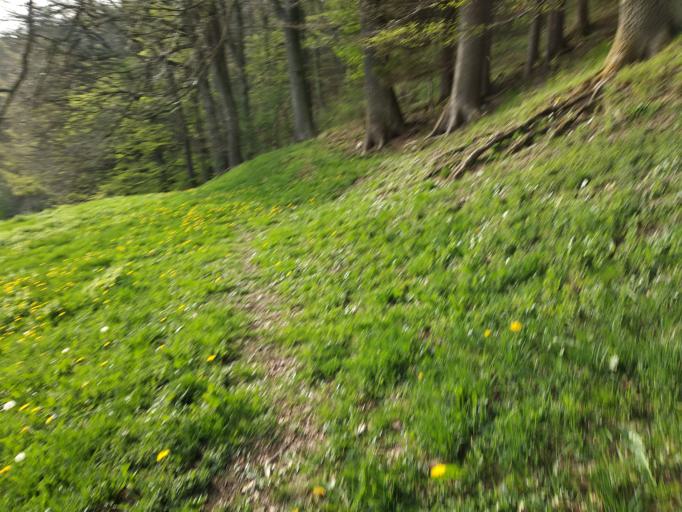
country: DE
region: Bavaria
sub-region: Swabia
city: Kronburg
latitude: 47.8996
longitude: 10.1472
